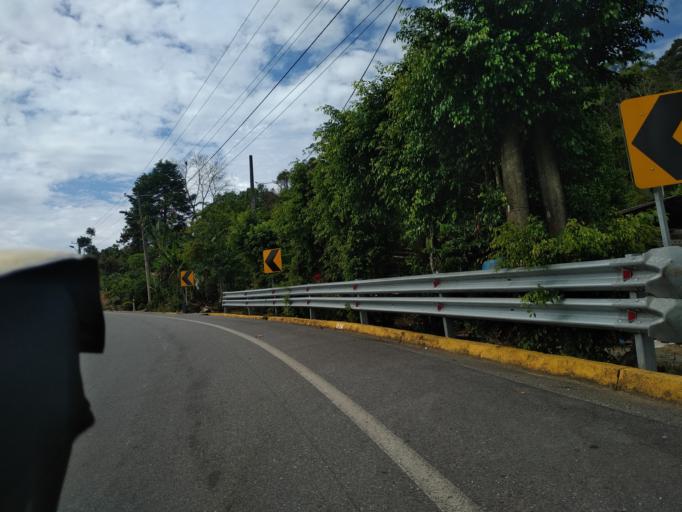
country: EC
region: Napo
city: Tena
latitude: -1.1216
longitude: -77.8105
